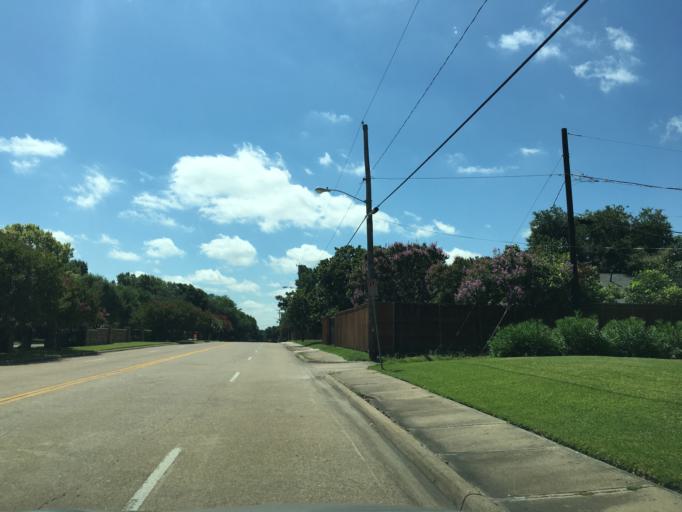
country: US
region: Texas
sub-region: Dallas County
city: Garland
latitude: 32.8394
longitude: -96.6503
